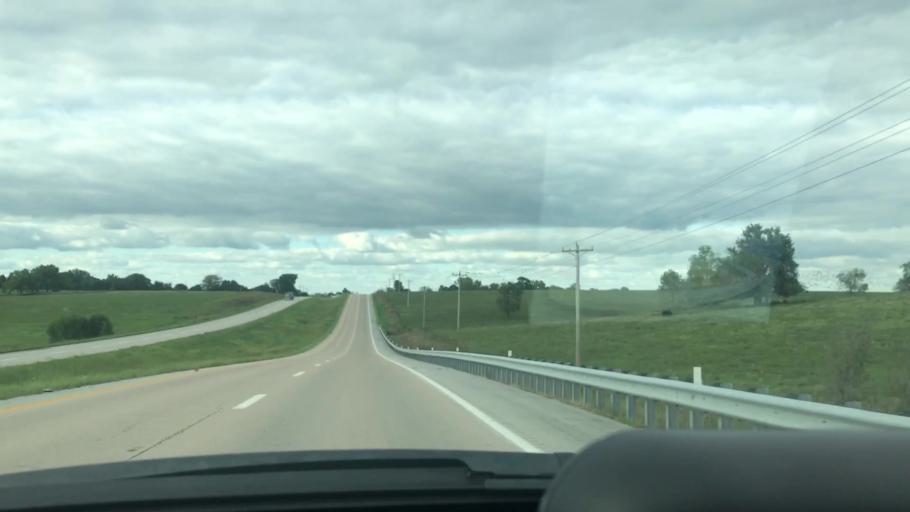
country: US
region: Missouri
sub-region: Benton County
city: Lincoln
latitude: 38.3237
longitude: -93.3419
